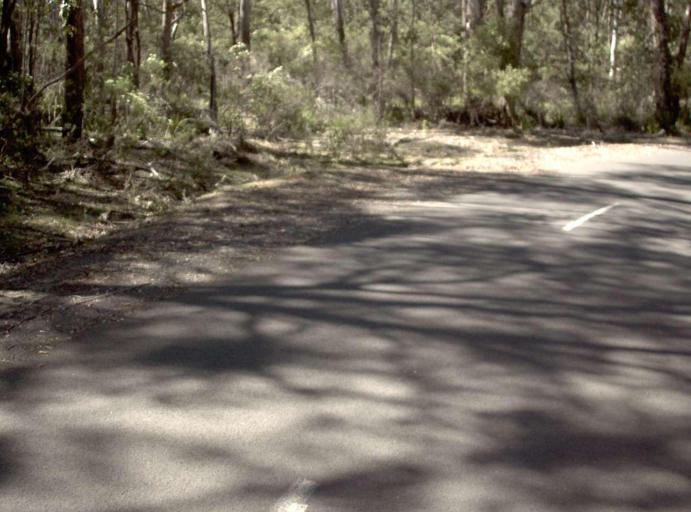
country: AU
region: New South Wales
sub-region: Bombala
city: Bombala
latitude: -37.1142
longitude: 148.7547
